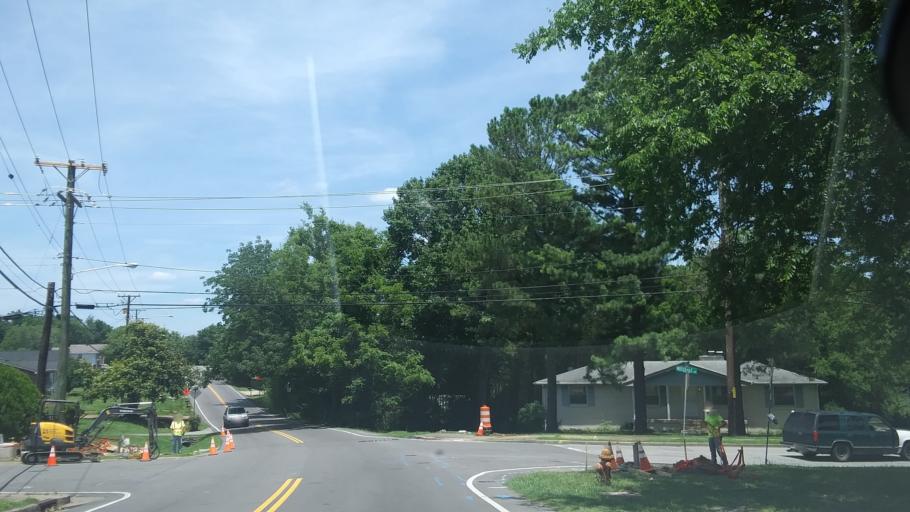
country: US
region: Tennessee
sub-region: Rutherford County
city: La Vergne
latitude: 36.0825
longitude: -86.6288
